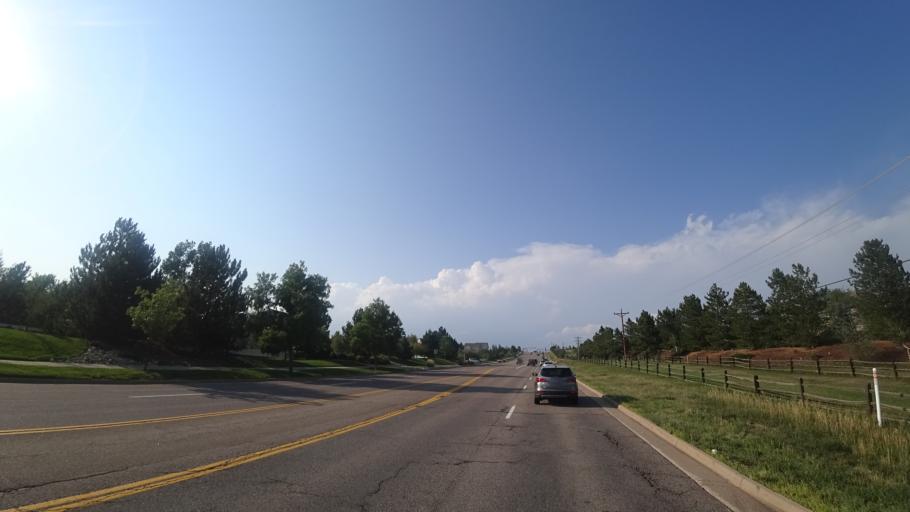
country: US
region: Colorado
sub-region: Douglas County
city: Parker
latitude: 39.6028
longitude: -104.7448
